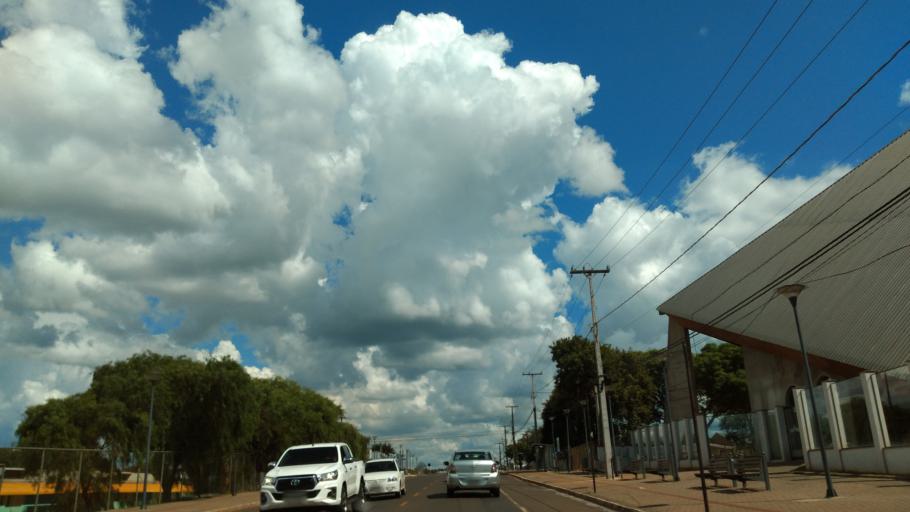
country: BR
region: Parana
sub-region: Guarapuava
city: Guarapuava
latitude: -25.4008
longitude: -51.4933
